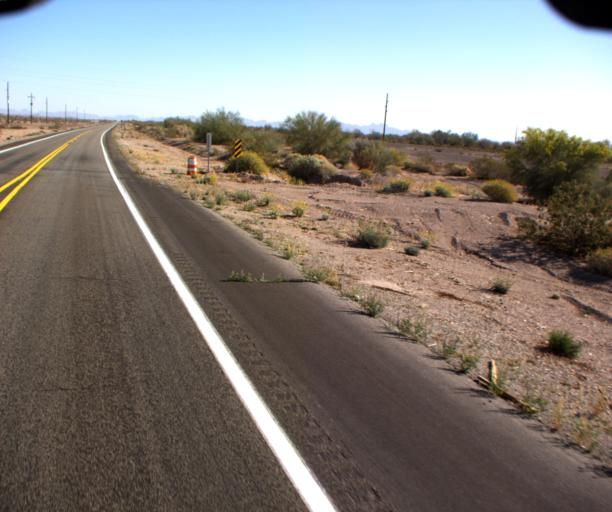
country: US
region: Arizona
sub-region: Yuma County
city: Fortuna Foothills
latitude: 32.8675
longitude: -114.3555
